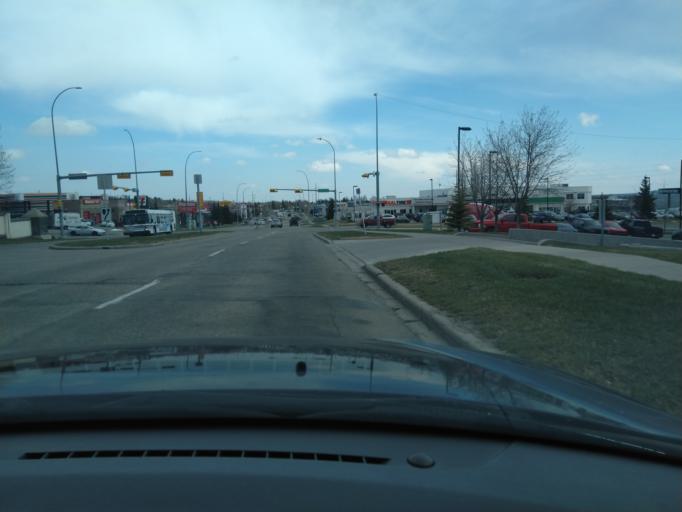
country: CA
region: Alberta
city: Calgary
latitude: 51.1269
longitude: -114.2102
